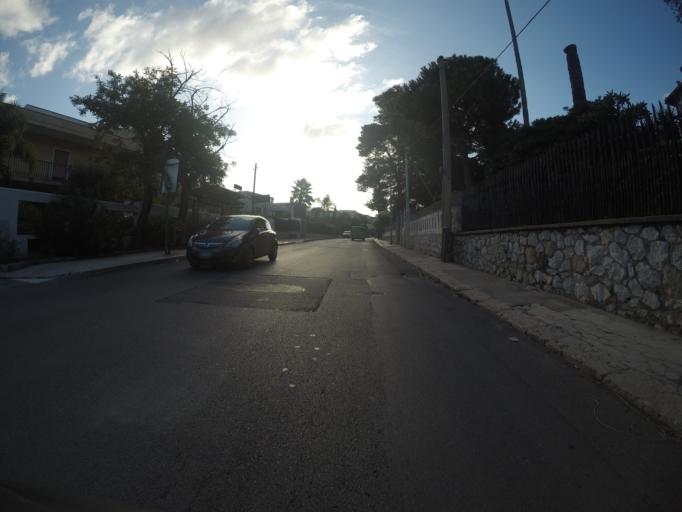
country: IT
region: Sicily
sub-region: Palermo
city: Isola delle Femmine
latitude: 38.1958
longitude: 13.2798
